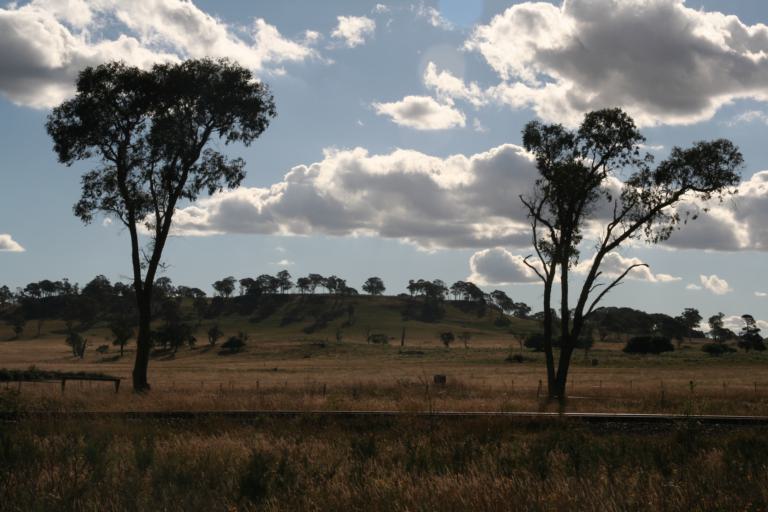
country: AU
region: New South Wales
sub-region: Guyra
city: Guyra
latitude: -30.1365
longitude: 151.6840
